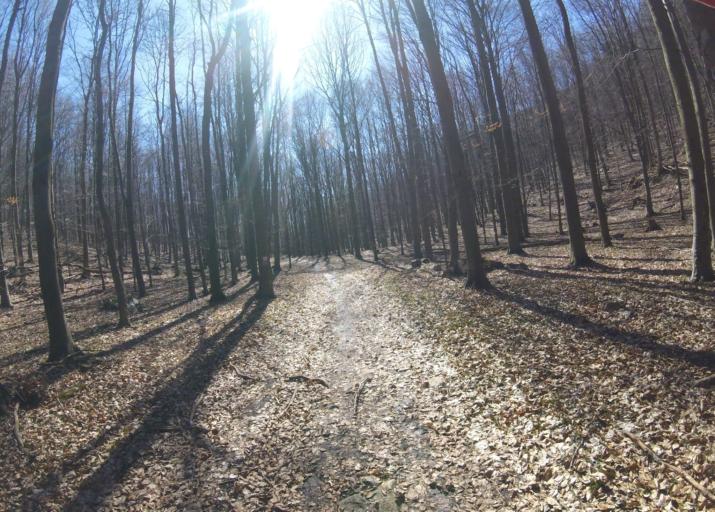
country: HU
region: Heves
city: Szilvasvarad
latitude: 48.0593
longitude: 20.4403
